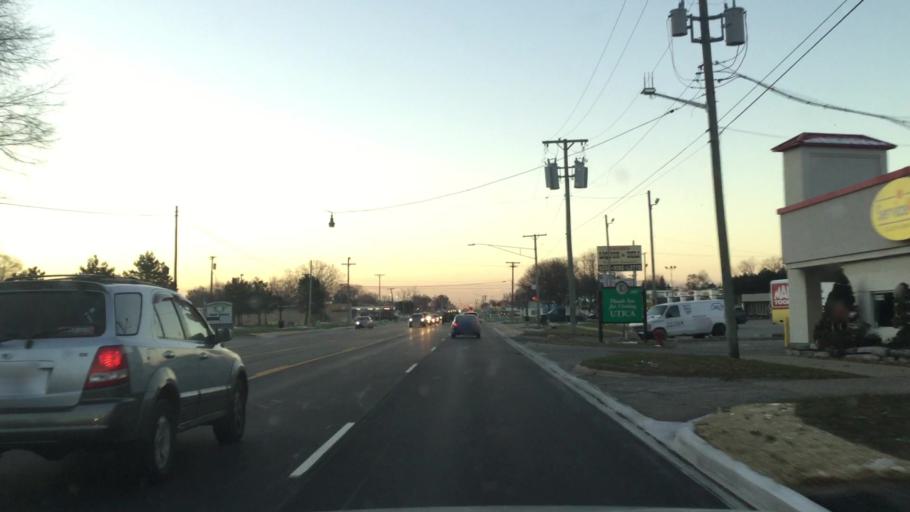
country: US
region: Michigan
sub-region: Macomb County
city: Utica
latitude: 42.6179
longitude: -83.0321
